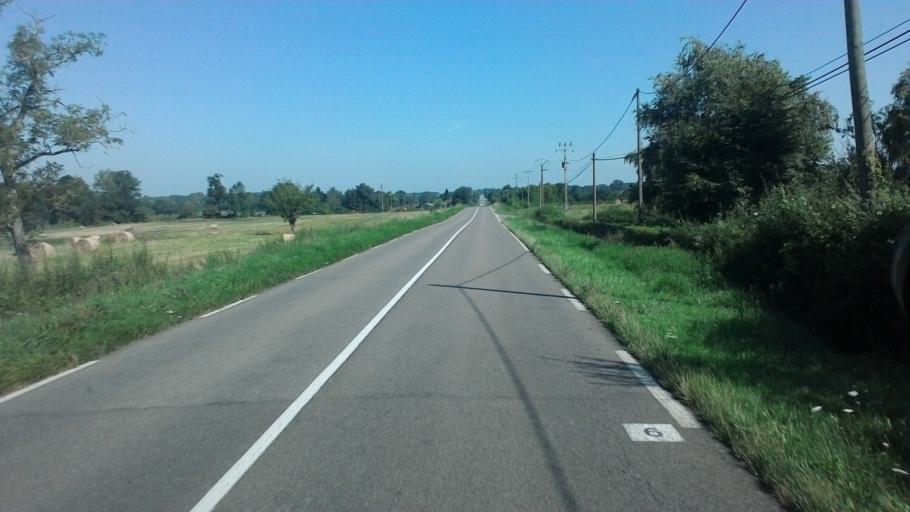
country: FR
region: Rhone-Alpes
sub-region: Departement de l'Ain
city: Saint-Trivier-de-Courtes
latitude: 46.4103
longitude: 5.1055
